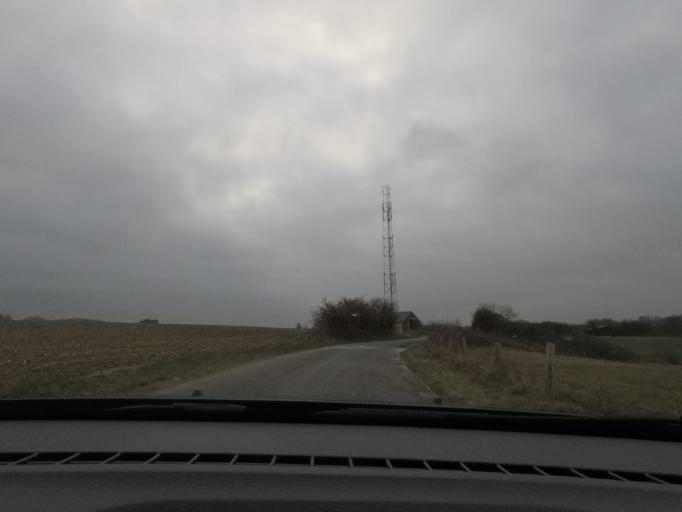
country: BE
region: Wallonia
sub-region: Province du Luxembourg
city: Habay-la-Vieille
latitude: 49.7144
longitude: 5.5866
